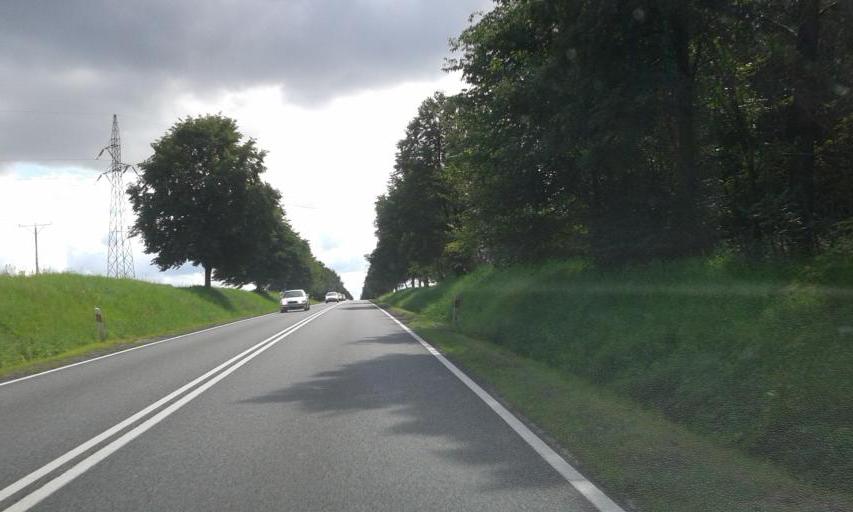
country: PL
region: West Pomeranian Voivodeship
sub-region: Powiat walecki
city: Walcz
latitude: 53.2560
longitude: 16.5100
